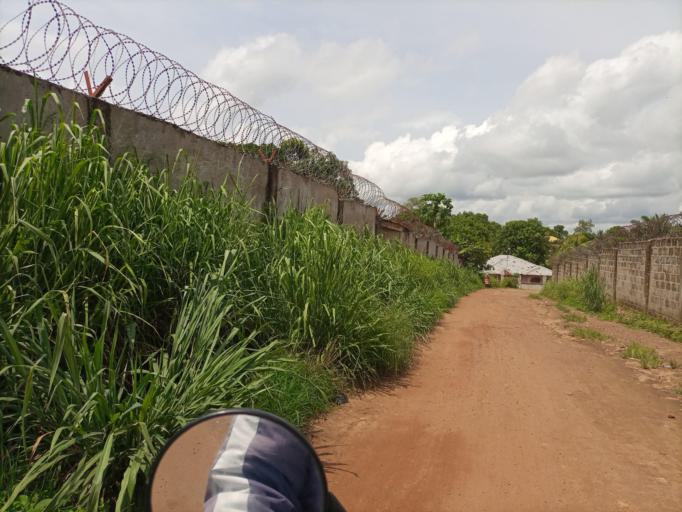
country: SL
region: Southern Province
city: Bo
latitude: 7.9715
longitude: -11.7628
